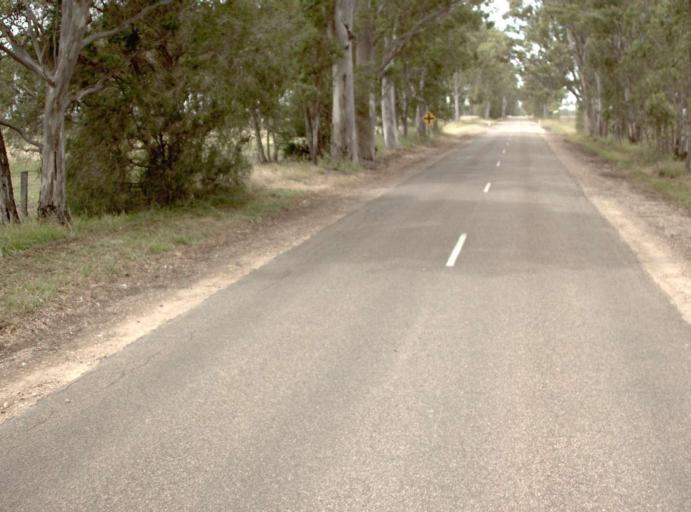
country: AU
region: Victoria
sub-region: Wellington
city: Sale
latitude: -37.8679
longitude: 147.0678
